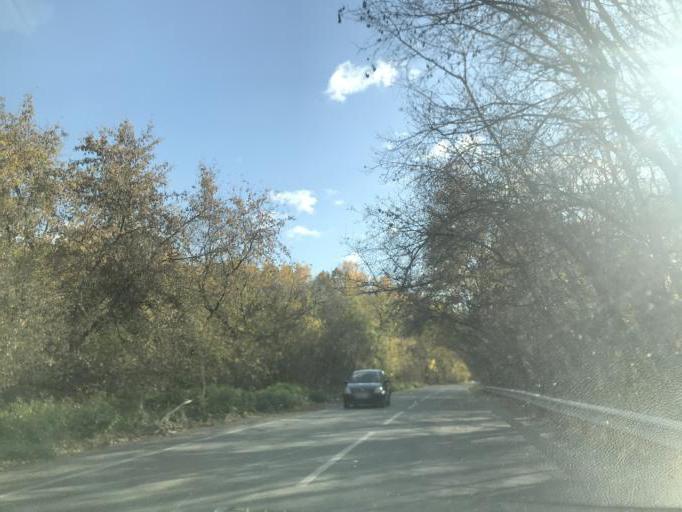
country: RU
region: Chelyabinsk
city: Dolgoderevenskoye
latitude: 55.2637
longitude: 61.3644
